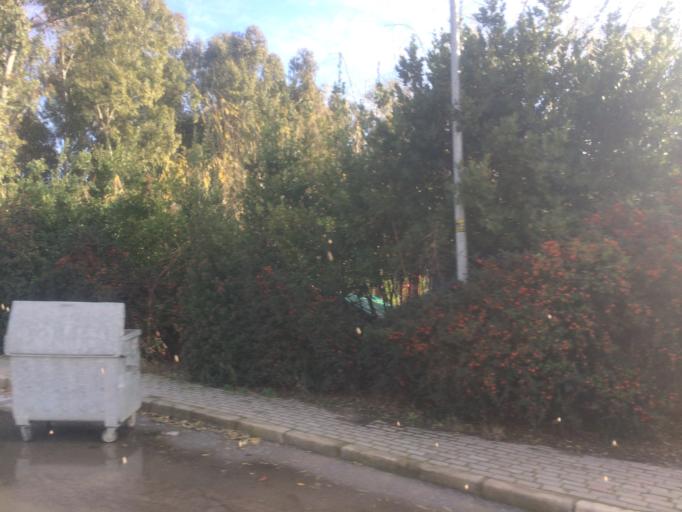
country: TR
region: Izmir
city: Karsiyaka
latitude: 38.4877
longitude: 26.9591
